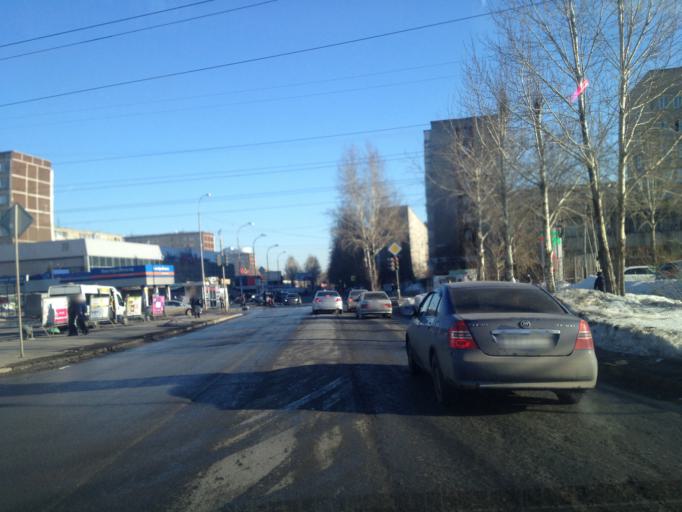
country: RU
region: Sverdlovsk
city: Yekaterinburg
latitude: 56.8701
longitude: 60.5514
